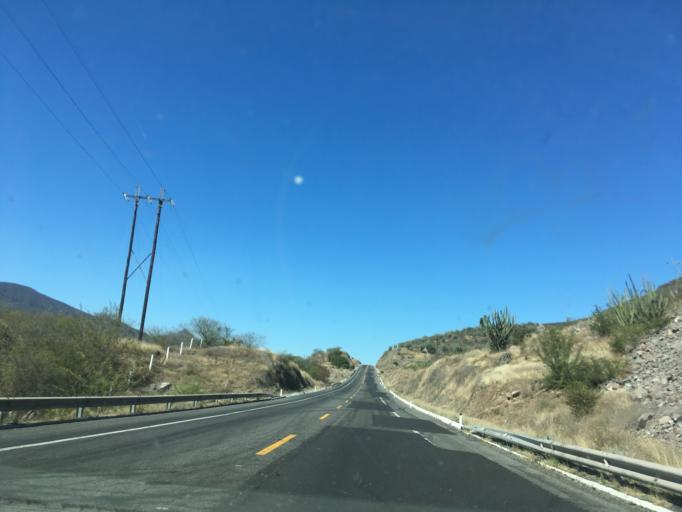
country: MX
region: Michoacan
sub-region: Arteaga
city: Las Canas
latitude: 18.5050
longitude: -101.9740
